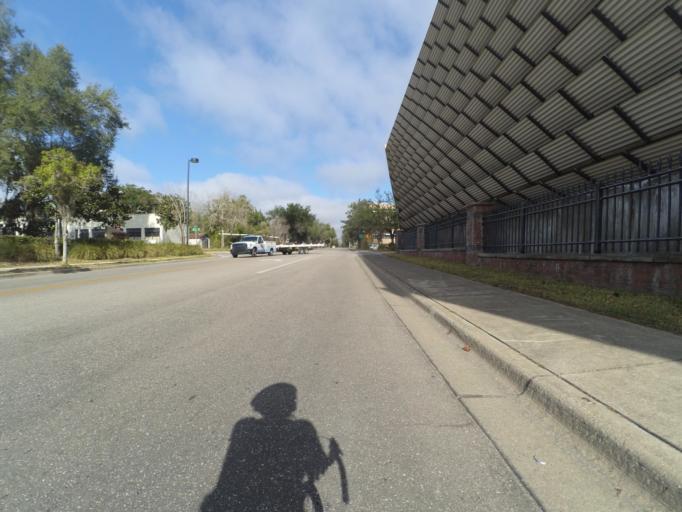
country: US
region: Florida
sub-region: Alachua County
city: Gainesville
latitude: 29.6467
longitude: -82.3222
